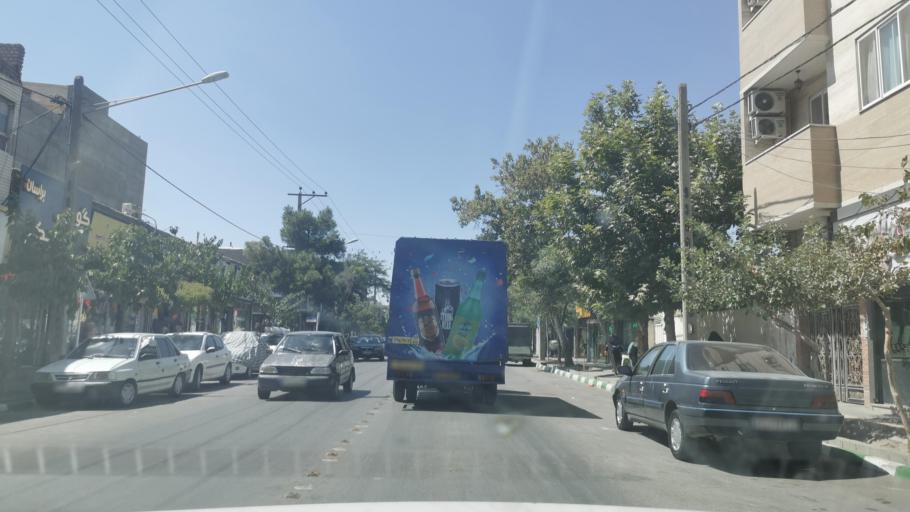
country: IR
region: Razavi Khorasan
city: Mashhad
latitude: 36.3588
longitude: 59.5479
